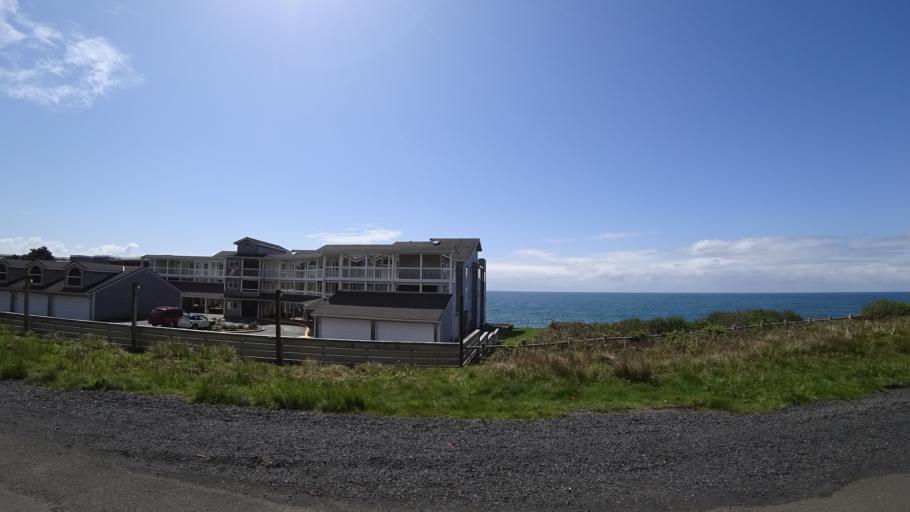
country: US
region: Oregon
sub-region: Lincoln County
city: Depoe Bay
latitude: 44.8262
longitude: -124.0659
